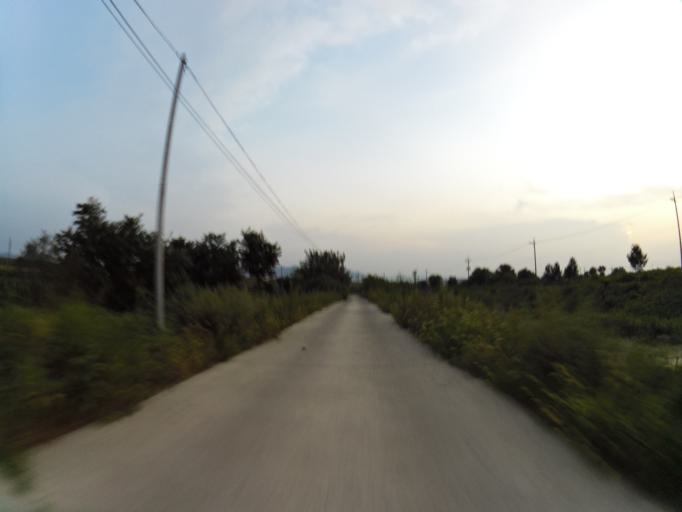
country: KR
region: Gyeongsangbuk-do
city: Gyeongsan-si
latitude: 35.8546
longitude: 128.7442
